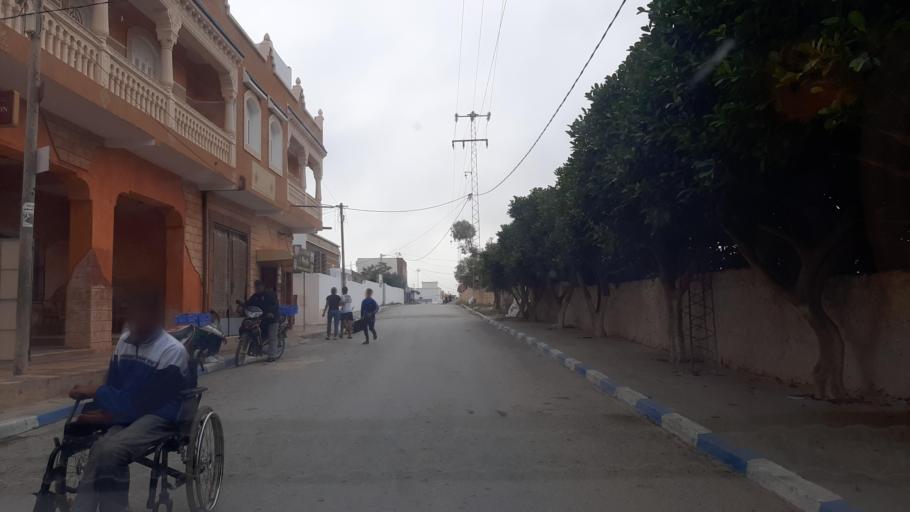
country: TN
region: Nabul
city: Menzel Heurr
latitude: 36.6807
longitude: 10.9256
